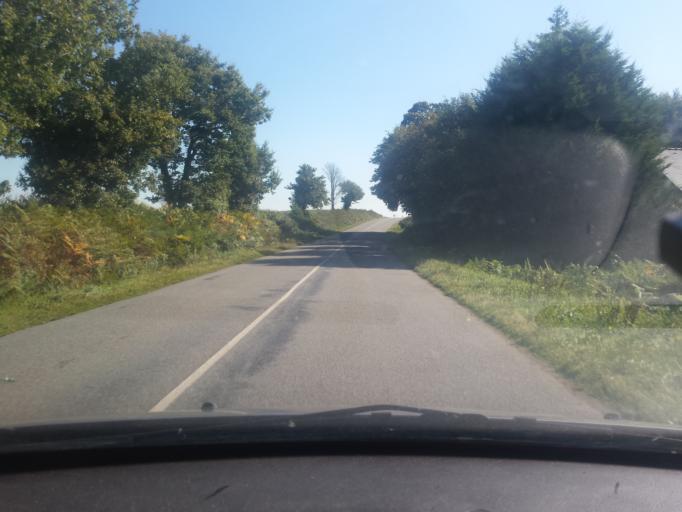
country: FR
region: Brittany
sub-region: Departement du Morbihan
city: Cleguerec
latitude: 48.1237
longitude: -3.1360
